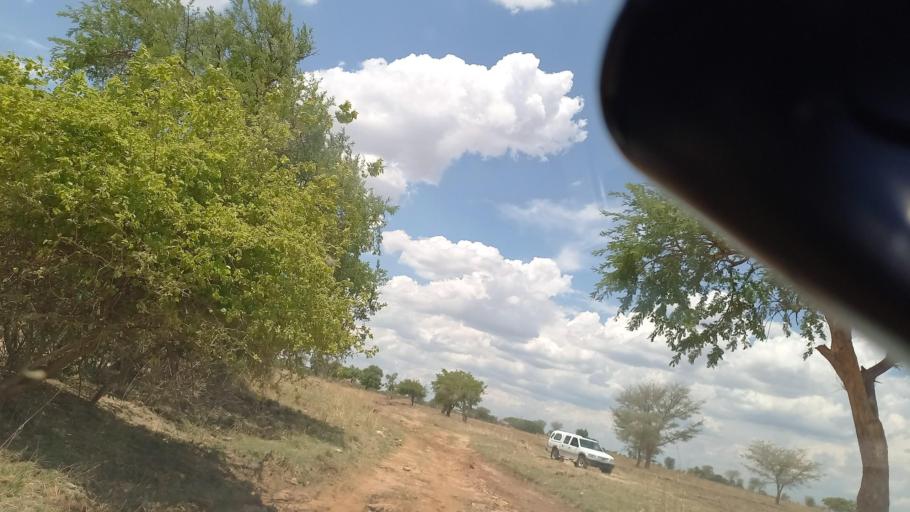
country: ZM
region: Southern
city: Mazabuka
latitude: -16.1144
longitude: 27.8140
